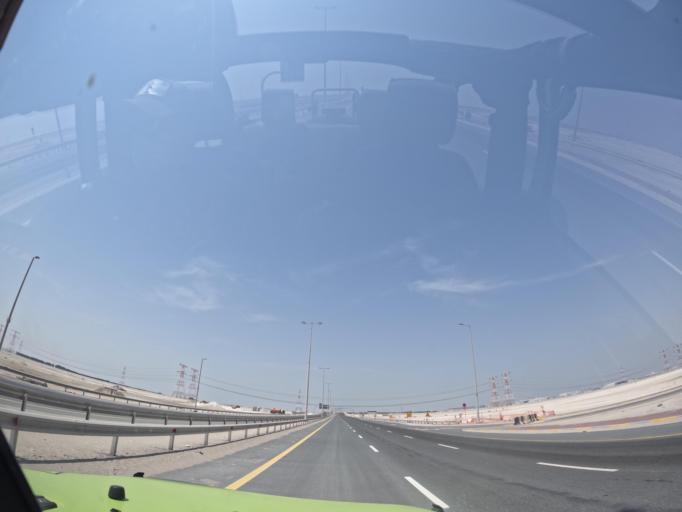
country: AE
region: Abu Dhabi
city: Abu Dhabi
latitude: 24.2510
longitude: 54.4687
